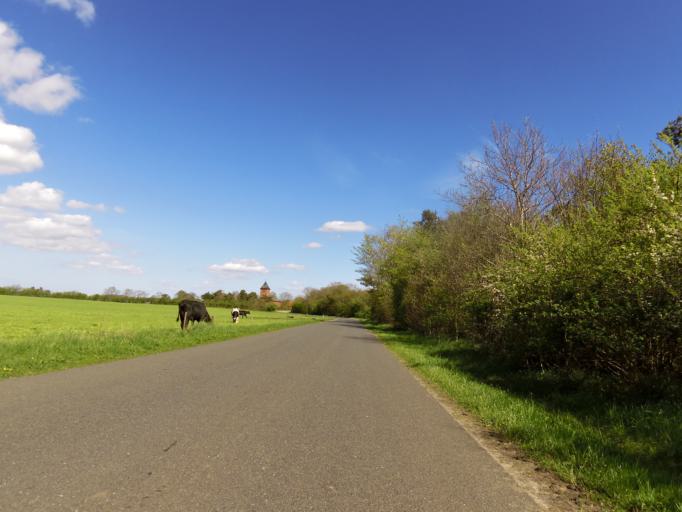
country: DK
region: Central Jutland
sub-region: Skive Kommune
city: Skive
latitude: 56.4602
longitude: 8.9711
